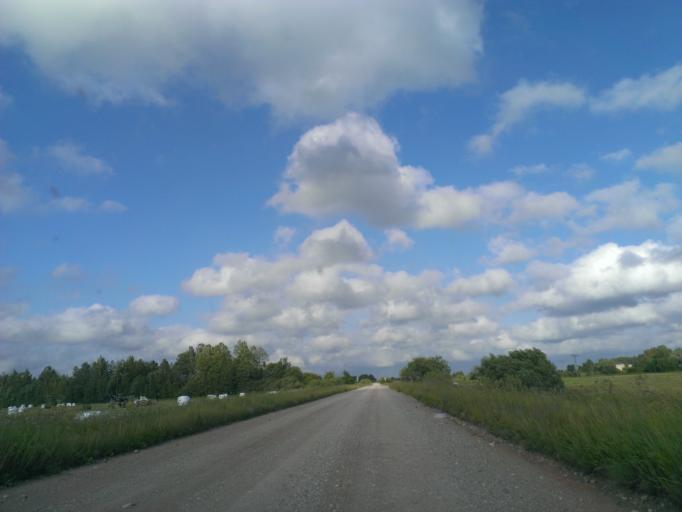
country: LV
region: Aizpute
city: Aizpute
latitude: 56.7527
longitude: 21.4367
